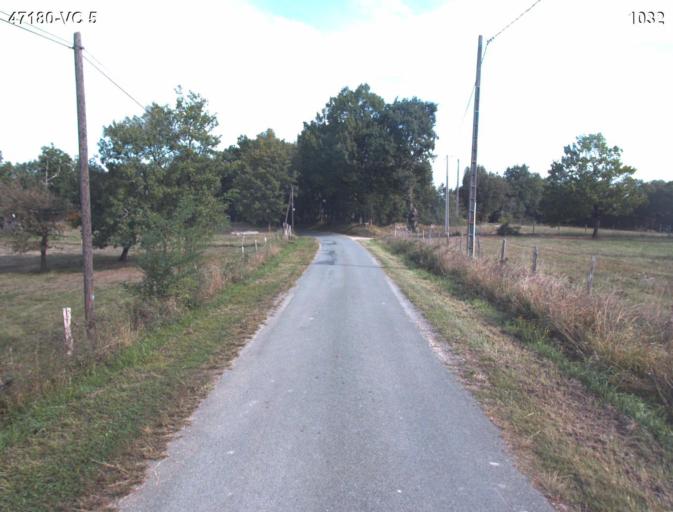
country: FR
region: Aquitaine
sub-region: Departement du Lot-et-Garonne
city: Sainte-Colombe-en-Bruilhois
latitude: 44.1739
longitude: 0.4686
